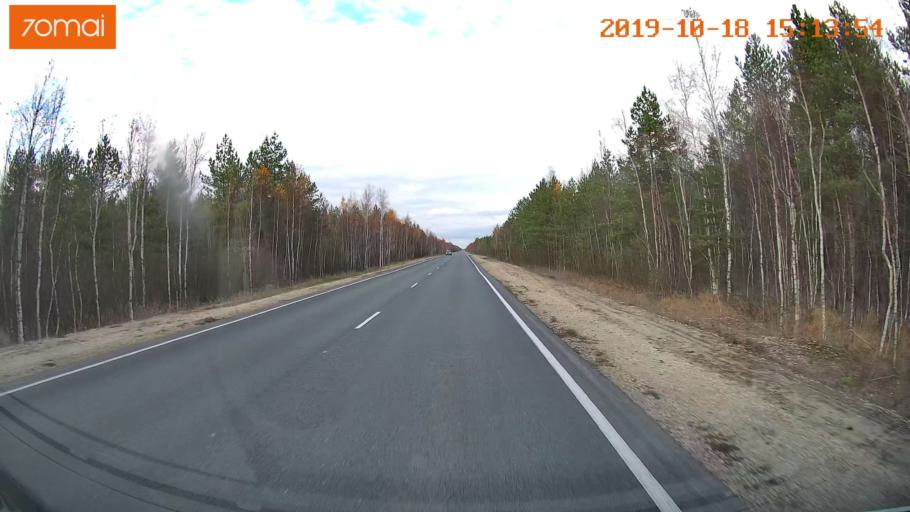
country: RU
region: Vladimir
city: Gus'-Khrustal'nyy
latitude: 55.5939
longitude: 40.7191
